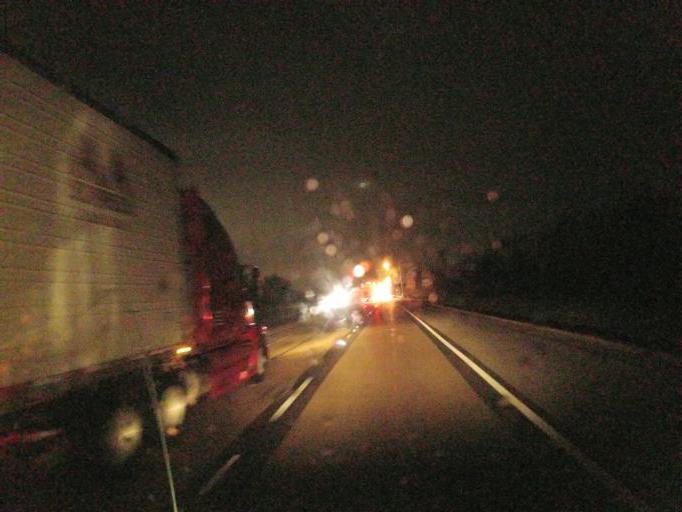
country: US
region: Illinois
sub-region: Madison County
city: Troy
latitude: 38.7542
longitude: -89.8895
